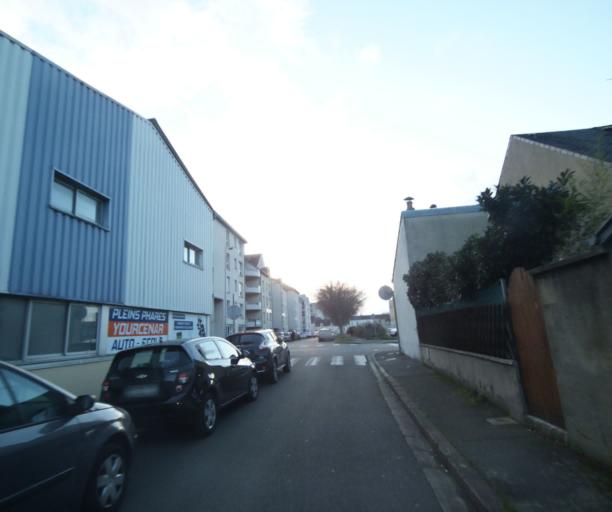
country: FR
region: Pays de la Loire
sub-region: Departement de la Sarthe
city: Le Mans
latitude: 47.9918
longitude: 0.1986
